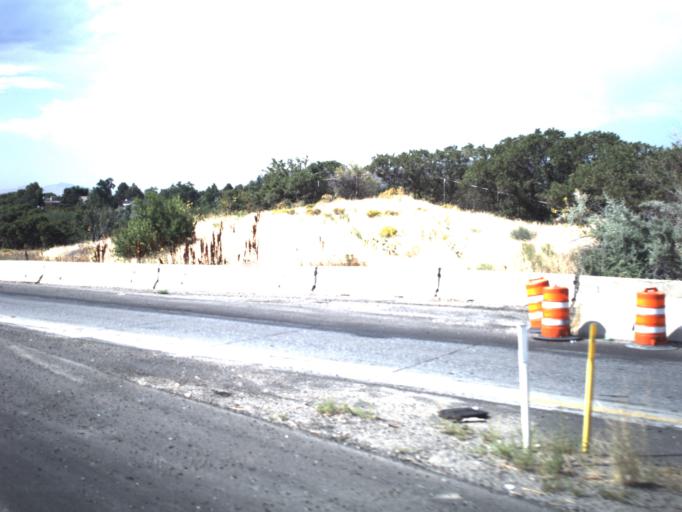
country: US
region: Utah
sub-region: Salt Lake County
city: Canyon Rim
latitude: 40.7135
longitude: -111.8239
